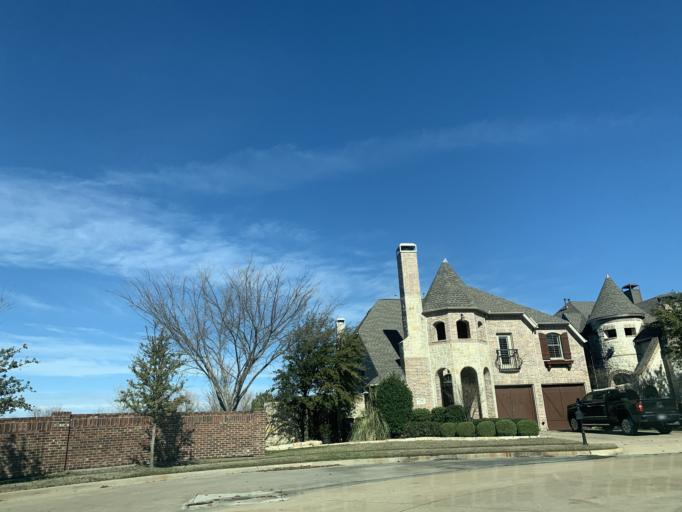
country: US
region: Texas
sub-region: Denton County
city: The Colony
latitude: 33.0729
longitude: -96.8552
